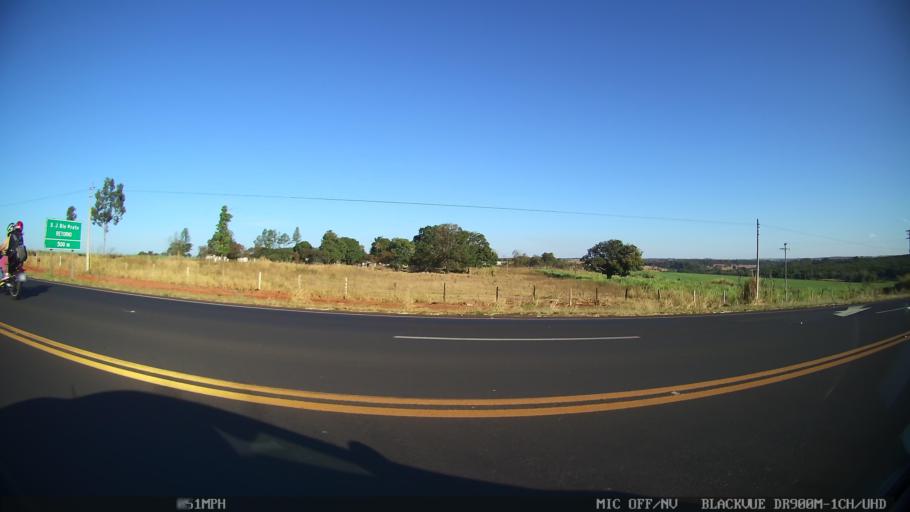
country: BR
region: Sao Paulo
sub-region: Guapiacu
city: Guapiacu
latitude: -20.7652
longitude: -49.1942
